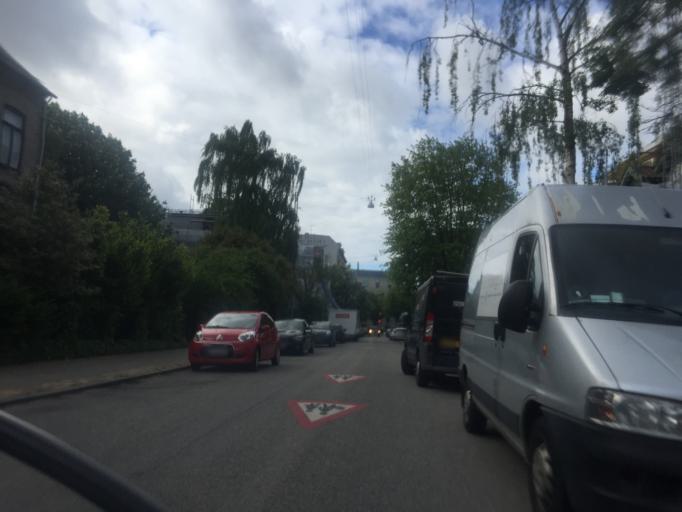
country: DK
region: Capital Region
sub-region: Frederiksberg Kommune
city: Frederiksberg
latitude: 55.6756
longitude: 12.5380
